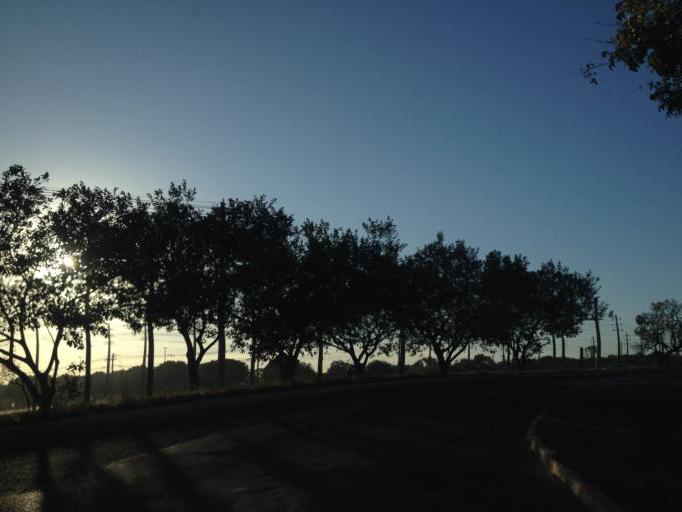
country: BR
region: Federal District
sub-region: Brasilia
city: Brasilia
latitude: -15.7561
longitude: -47.9282
